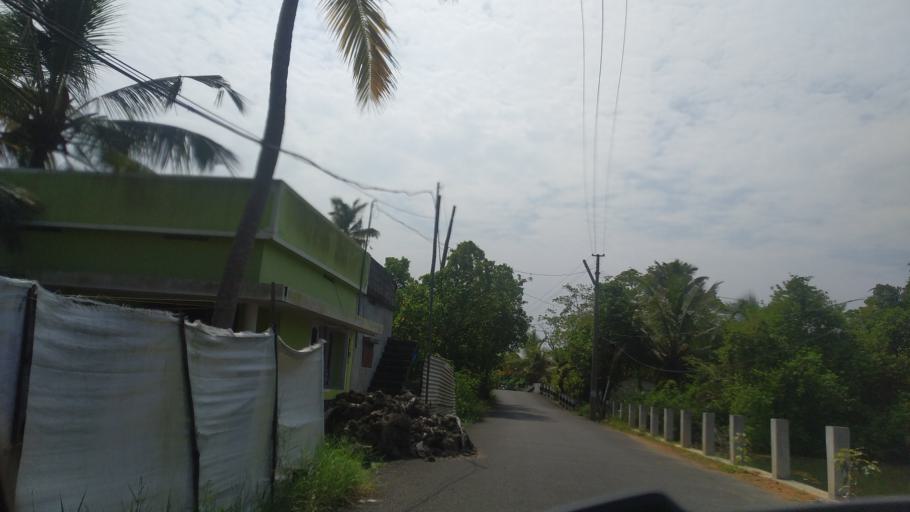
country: IN
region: Kerala
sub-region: Ernakulam
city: Elur
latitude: 10.0442
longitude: 76.2112
